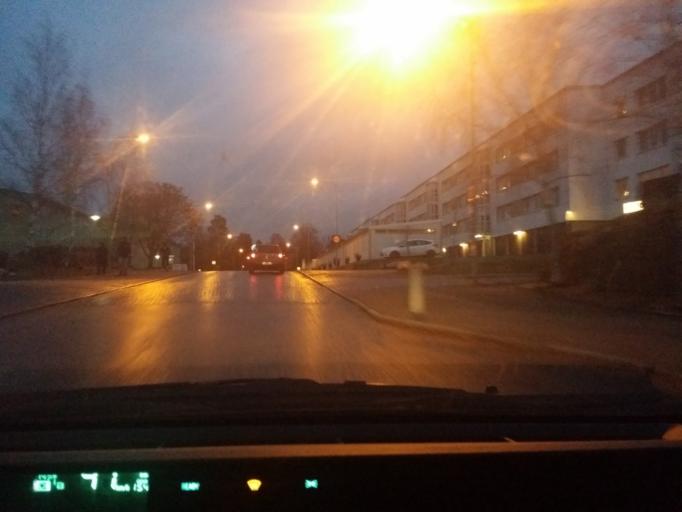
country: SE
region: Vaestmanland
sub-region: Vasteras
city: Vasteras
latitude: 59.6095
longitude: 16.5753
